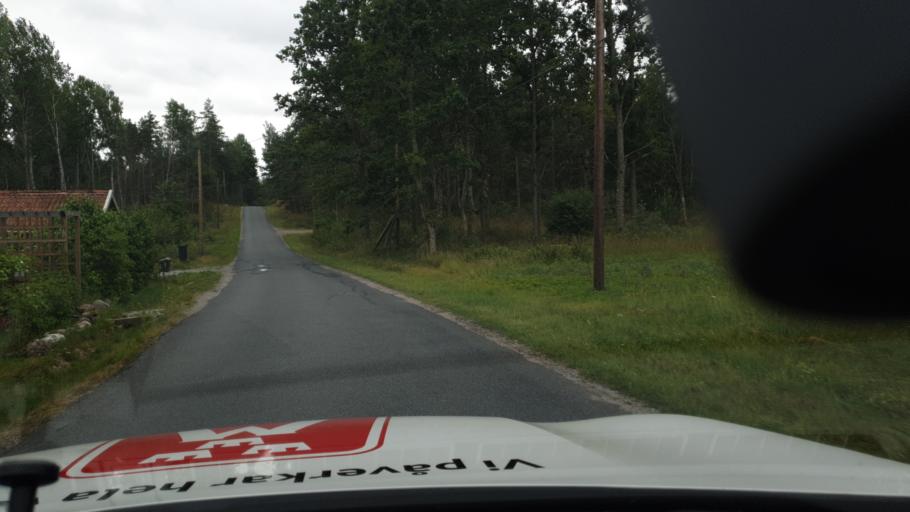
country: SE
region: Soedermanland
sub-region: Strangnas Kommun
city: Akers Styckebruk
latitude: 59.1856
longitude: 17.1358
